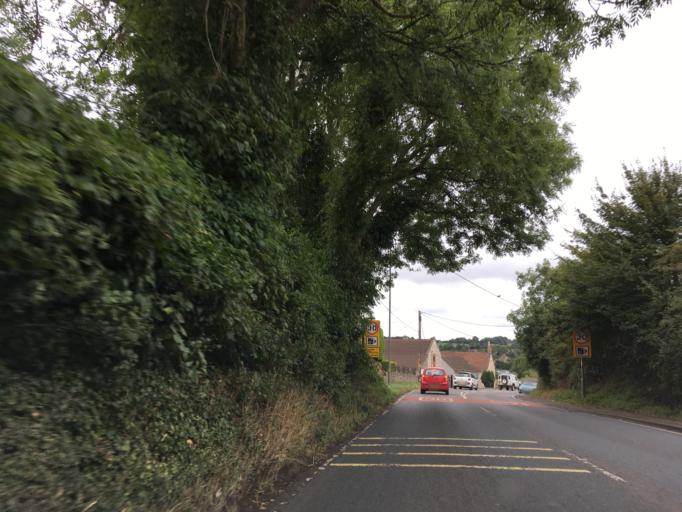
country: GB
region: England
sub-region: Bath and North East Somerset
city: Timsbury
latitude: 51.3488
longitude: -2.4842
